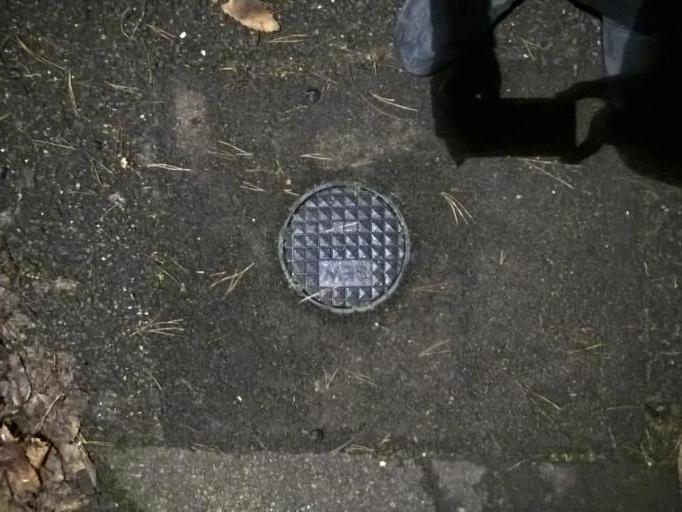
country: GB
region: England
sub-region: Bracknell Forest
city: Bracknell
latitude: 51.4040
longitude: -0.7449
